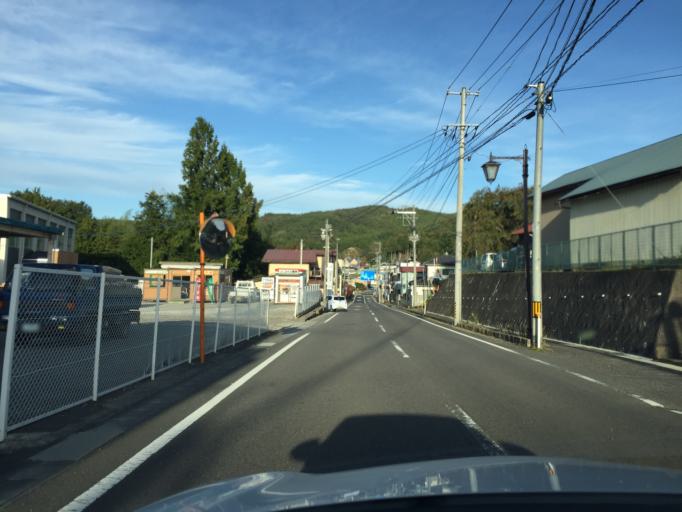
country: JP
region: Fukushima
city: Ishikawa
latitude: 37.2393
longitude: 140.5661
